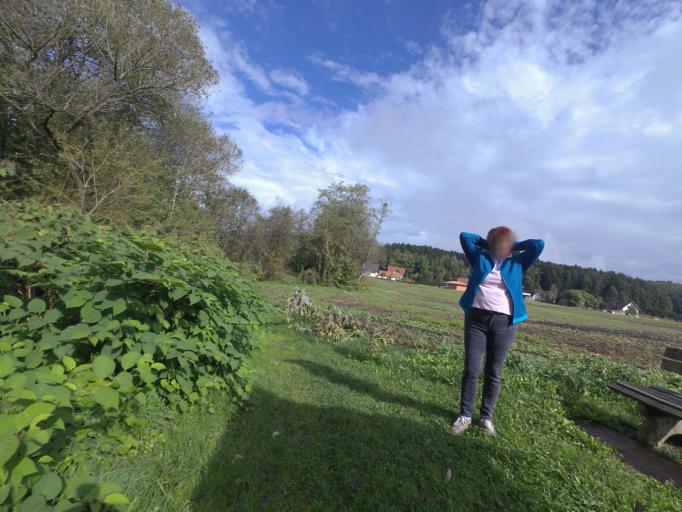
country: AT
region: Styria
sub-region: Politischer Bezirk Deutschlandsberg
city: Sankt Martin im Sulmtal
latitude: 46.7591
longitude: 15.3008
